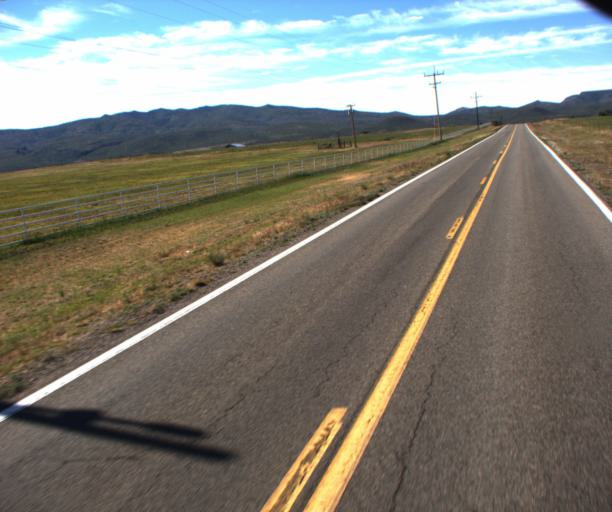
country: US
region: Arizona
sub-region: Yavapai County
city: Congress
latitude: 34.2888
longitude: -112.7229
